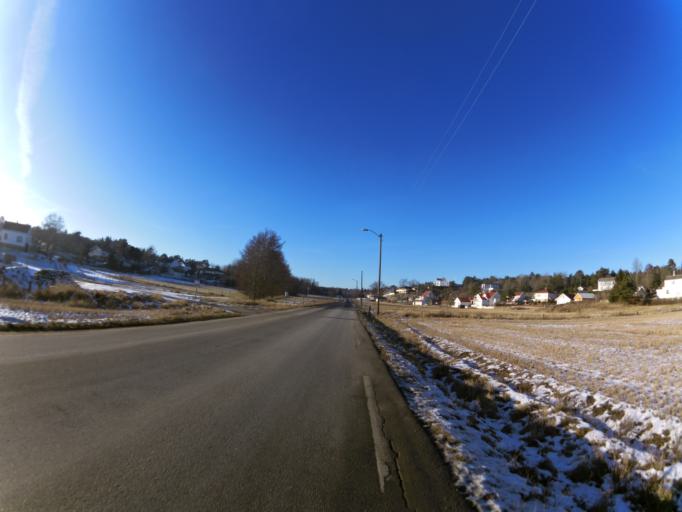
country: NO
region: Ostfold
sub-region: Fredrikstad
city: Lervik
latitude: 59.1974
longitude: 10.8214
